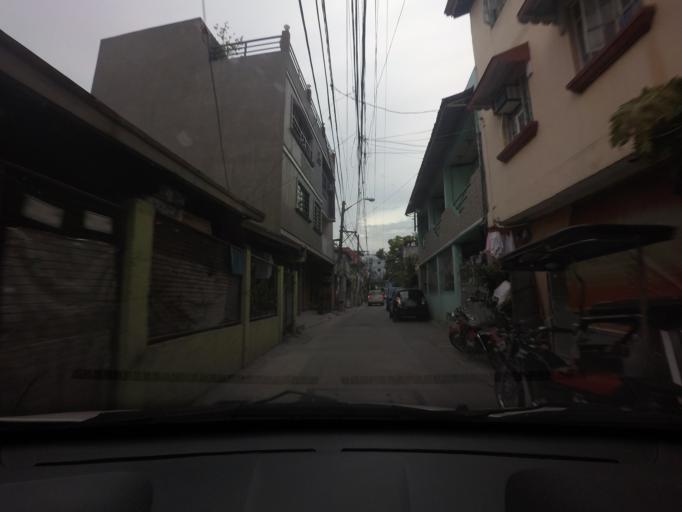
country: PH
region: Calabarzon
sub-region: Province of Rizal
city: Pateros
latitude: 14.5391
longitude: 121.0616
